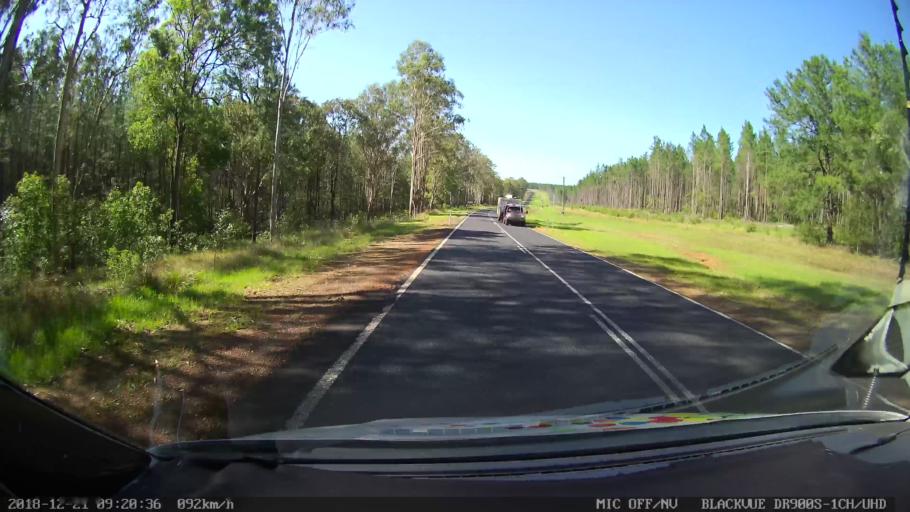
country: AU
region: New South Wales
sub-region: Clarence Valley
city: Maclean
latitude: -29.3170
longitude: 153.0002
